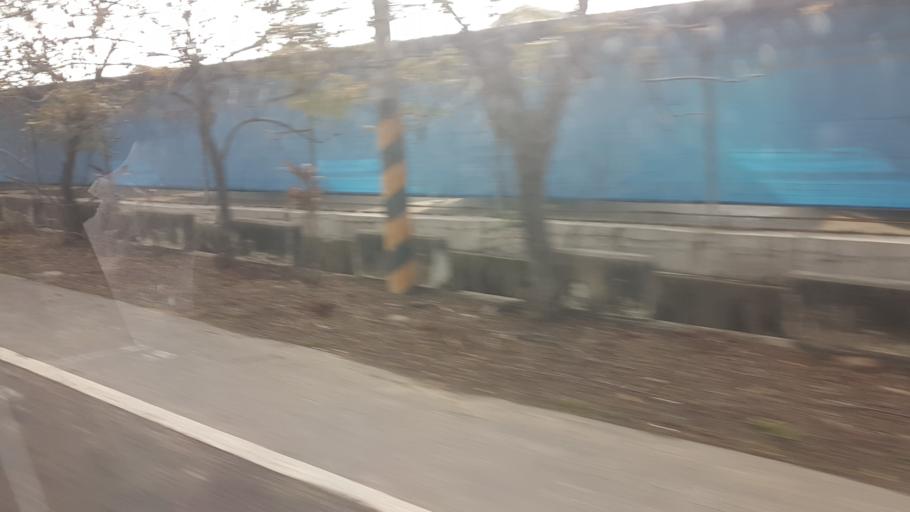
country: TW
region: Taiwan
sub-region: Chiayi
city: Jiayi Shi
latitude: 23.4005
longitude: 120.4285
